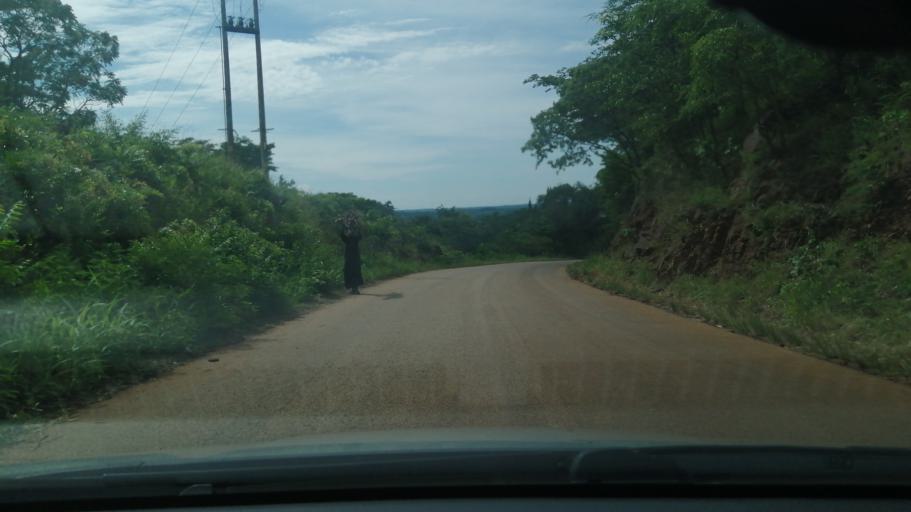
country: ZW
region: Mashonaland West
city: Norton
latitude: -17.8613
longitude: 30.7965
